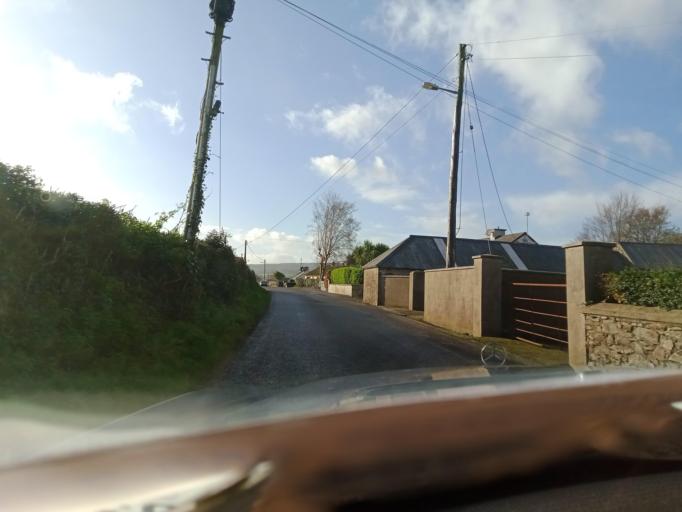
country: IE
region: Leinster
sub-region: Kilkenny
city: Mooncoin
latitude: 52.3285
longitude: -7.2822
